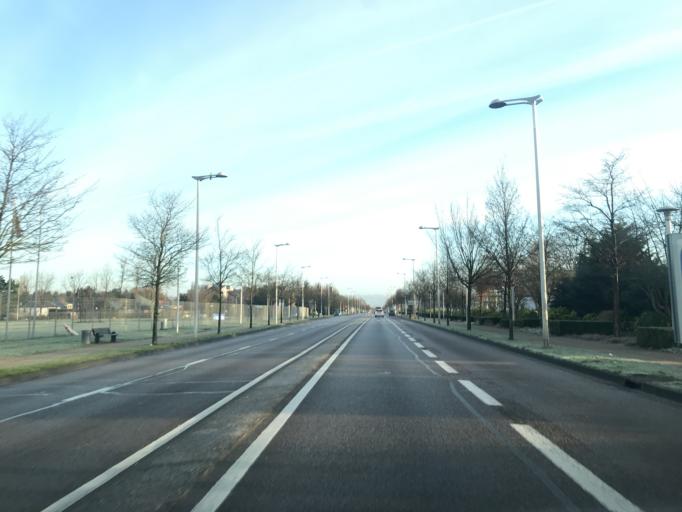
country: FR
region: Haute-Normandie
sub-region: Departement de la Seine-Maritime
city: Le Grand-Quevilly
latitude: 49.3939
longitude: 1.0595
